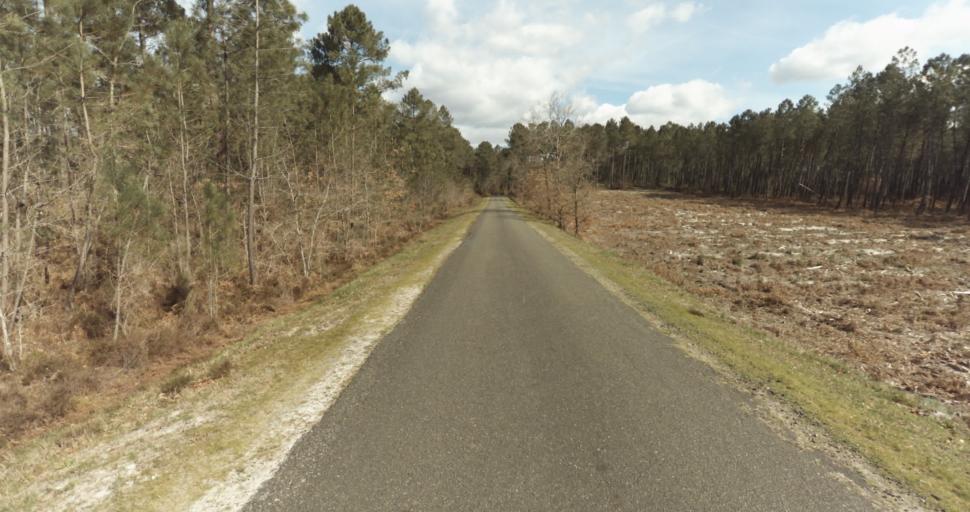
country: FR
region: Aquitaine
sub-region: Departement des Landes
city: Roquefort
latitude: 44.0512
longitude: -0.3596
